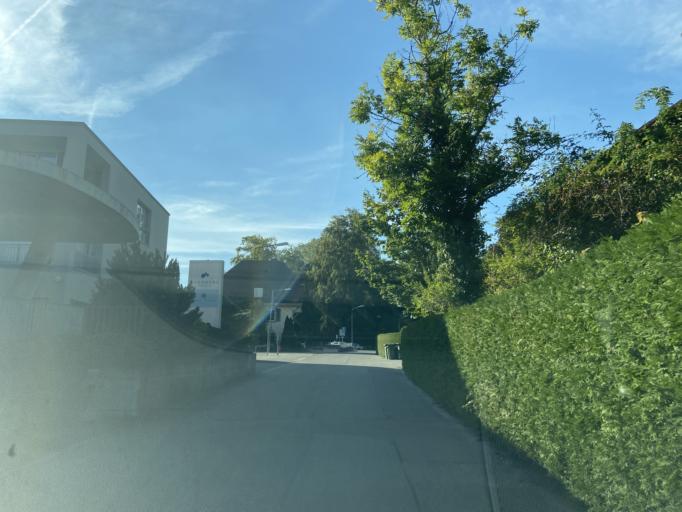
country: CH
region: Zurich
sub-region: Bezirk Winterthur
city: Stadt Winterthur (Kreis 1) / Lind
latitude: 47.5103
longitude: 8.7306
